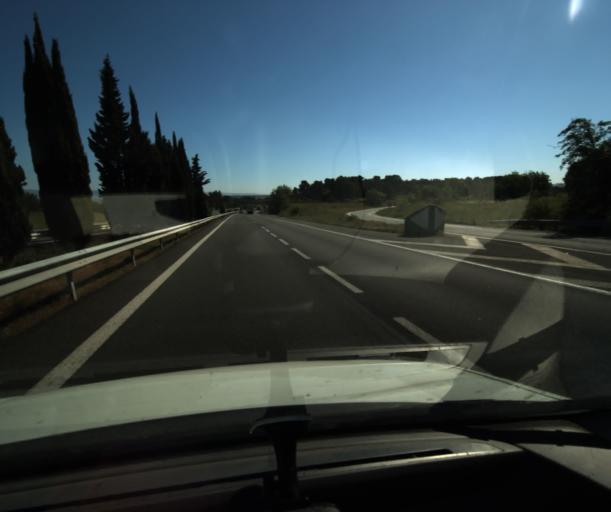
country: FR
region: Languedoc-Roussillon
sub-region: Departement de l'Aude
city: Trebes
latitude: 43.1932
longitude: 2.4174
